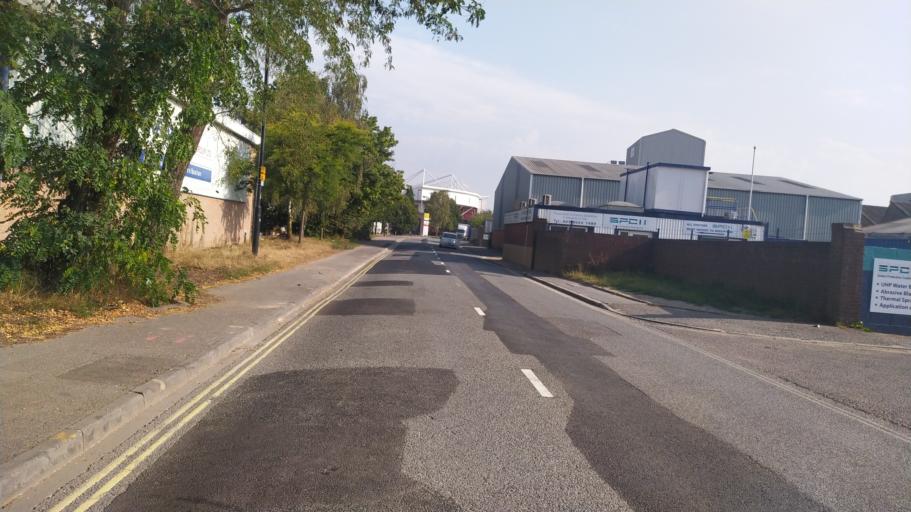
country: GB
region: England
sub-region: Southampton
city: Southampton
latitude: 50.9026
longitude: -1.3908
